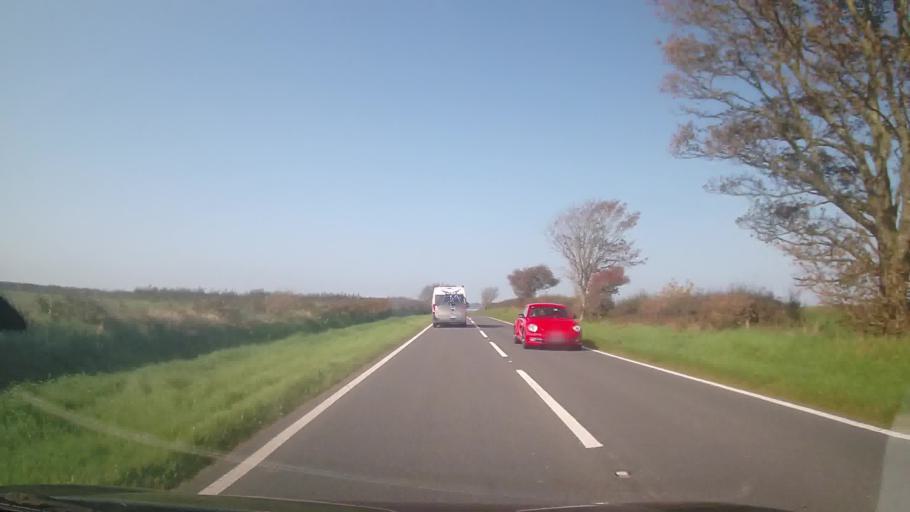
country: GB
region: Wales
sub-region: County of Ceredigion
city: Cardigan
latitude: 52.0274
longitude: -4.6923
